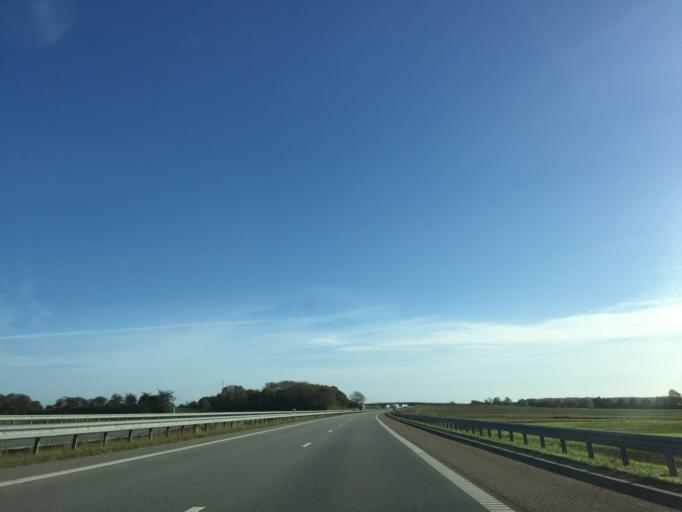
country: DK
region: South Denmark
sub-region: Sonderborg Kommune
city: Grasten
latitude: 54.9592
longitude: 9.5970
